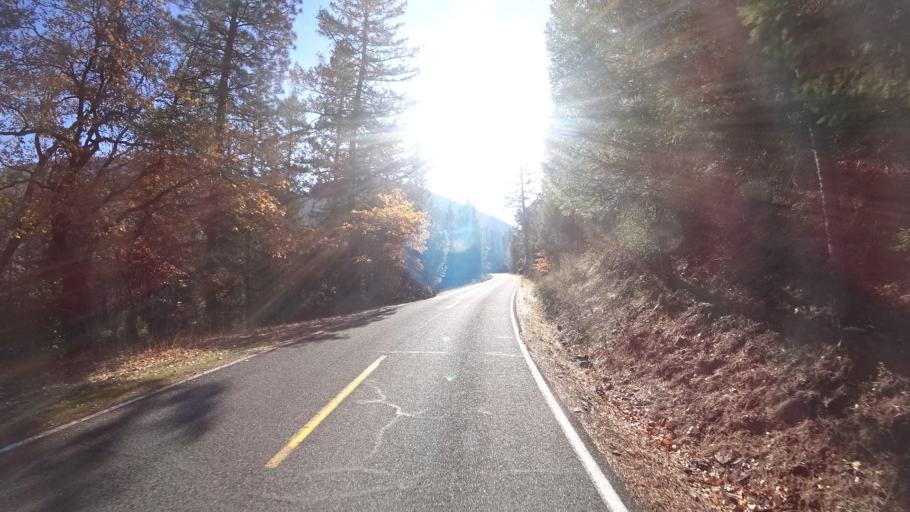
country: US
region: California
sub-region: Siskiyou County
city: Yreka
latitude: 41.8940
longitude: -122.8250
